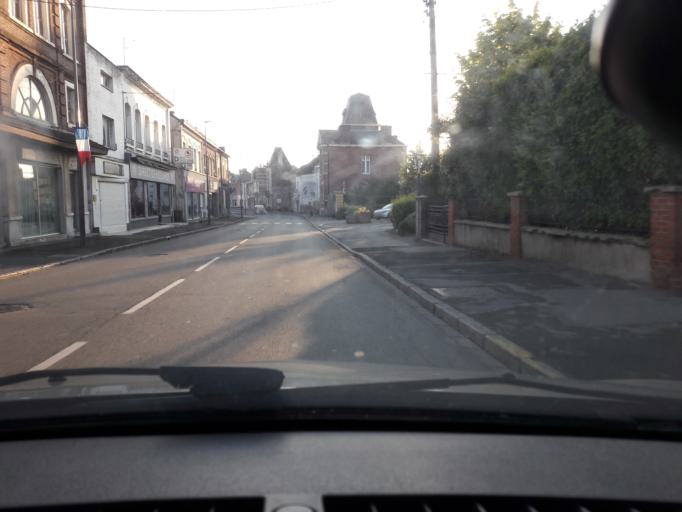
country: FR
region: Nord-Pas-de-Calais
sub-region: Departement du Nord
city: Jeumont
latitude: 50.2961
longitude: 4.0964
